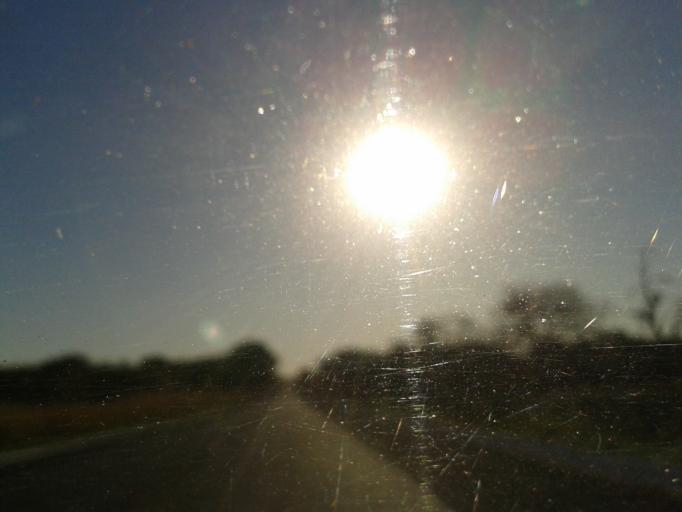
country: BR
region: Minas Gerais
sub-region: Santa Vitoria
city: Santa Vitoria
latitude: -19.1255
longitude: -50.2749
